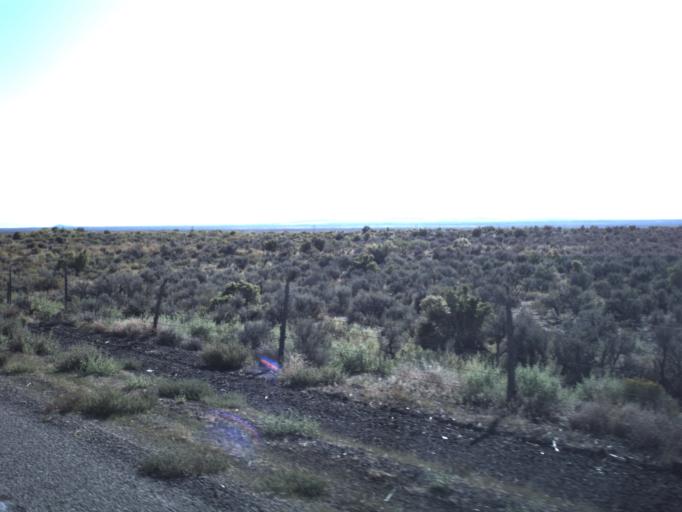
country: US
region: Utah
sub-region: Millard County
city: Fillmore
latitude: 39.1686
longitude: -112.4101
